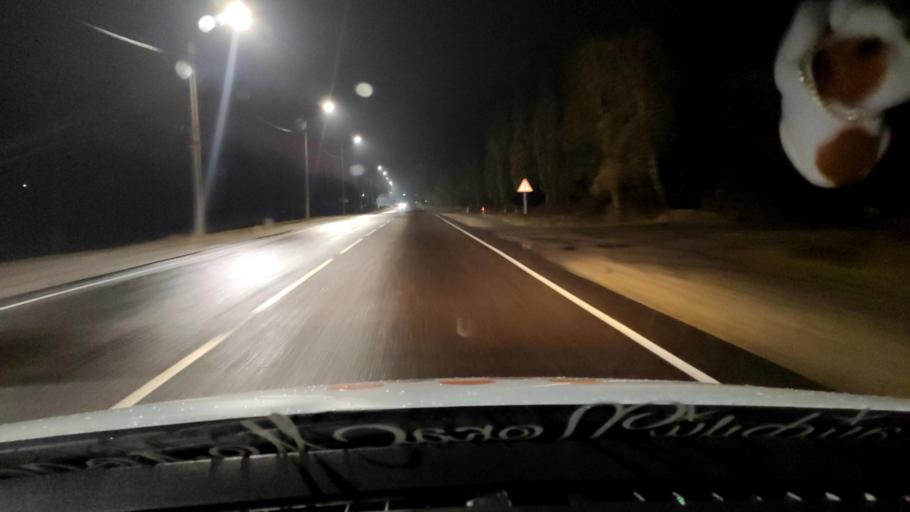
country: RU
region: Voronezj
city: Semiluki
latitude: 51.7122
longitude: 39.0268
